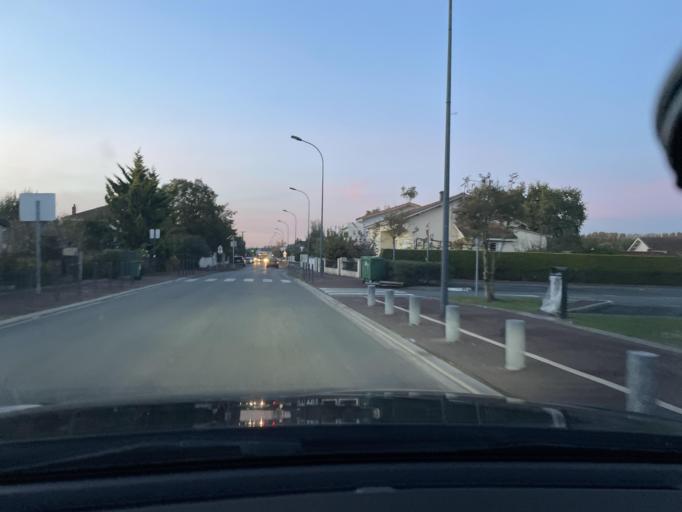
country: FR
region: Aquitaine
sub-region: Departement de la Gironde
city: Le Bouscat
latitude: 44.8808
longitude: -0.5918
